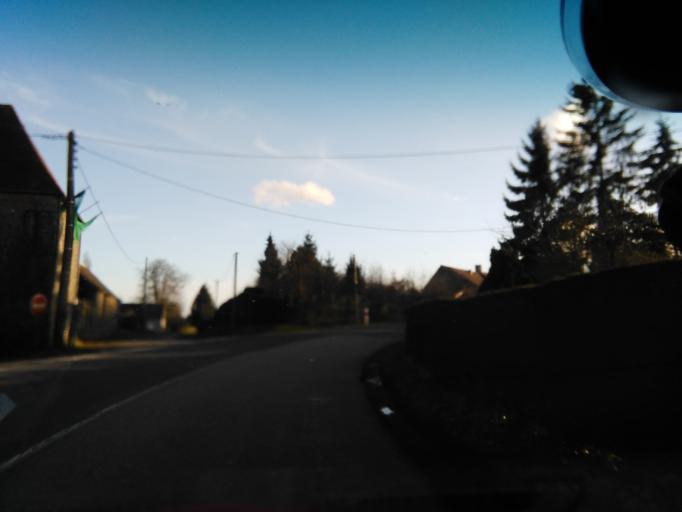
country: FR
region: Lower Normandy
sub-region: Departement de l'Orne
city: Pont-Ecrepin
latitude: 48.7184
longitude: -0.2693
